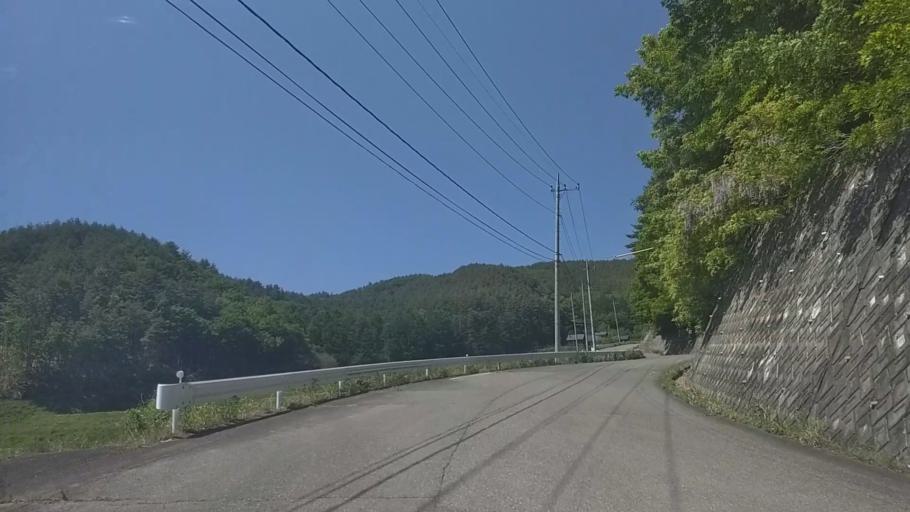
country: JP
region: Yamanashi
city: Nirasaki
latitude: 35.8577
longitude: 138.4473
